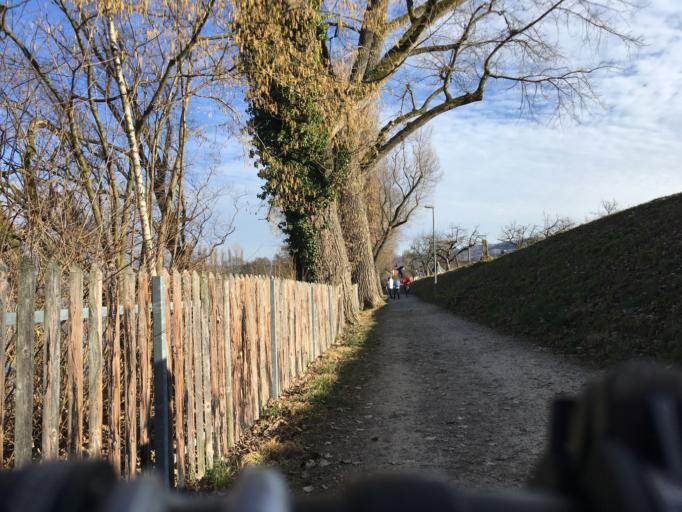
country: CH
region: Schaffhausen
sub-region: Bezirk Stein
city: Stein am Rhein
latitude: 47.6546
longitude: 8.8631
